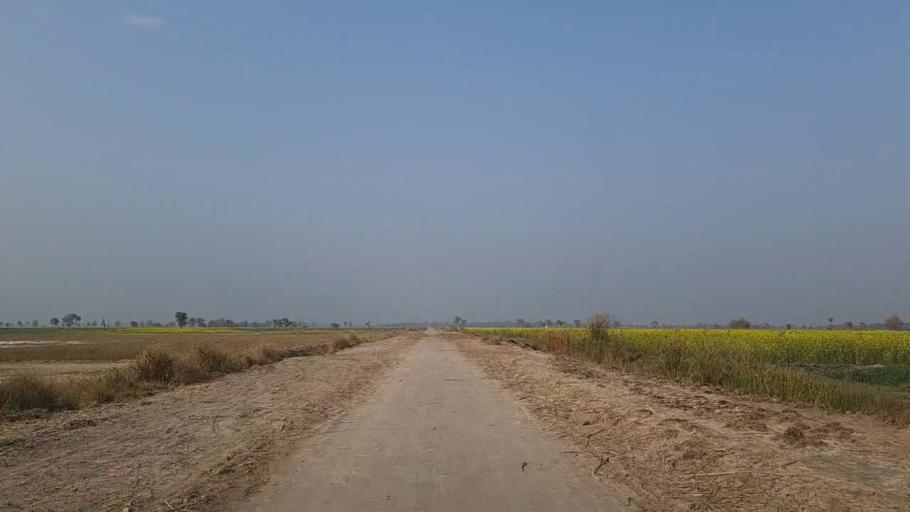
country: PK
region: Sindh
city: Jam Sahib
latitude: 26.3352
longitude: 68.5148
